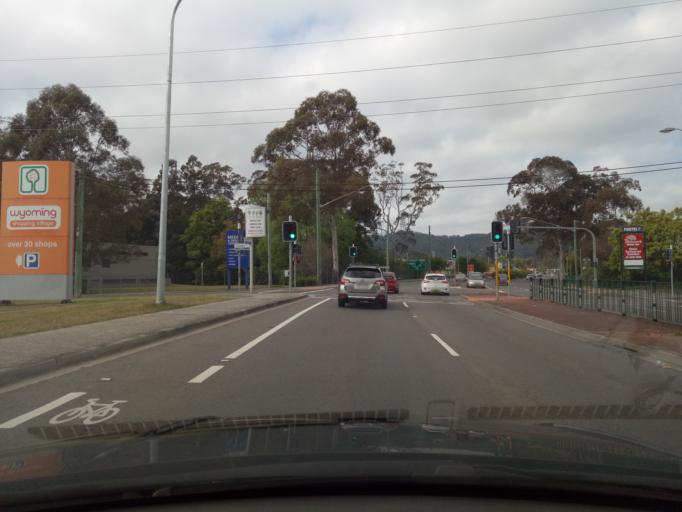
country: AU
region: New South Wales
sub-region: Gosford Shire
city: Narara
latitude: -33.4054
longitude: 151.3511
